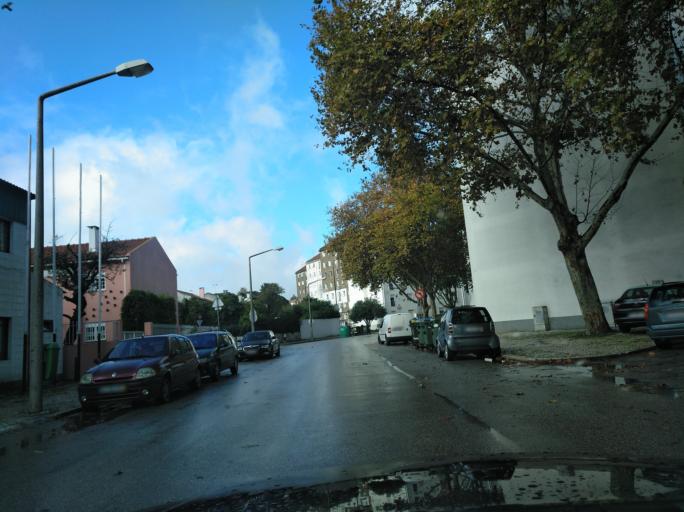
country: PT
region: Lisbon
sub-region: Loures
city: Moscavide
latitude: 38.7587
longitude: -9.1092
